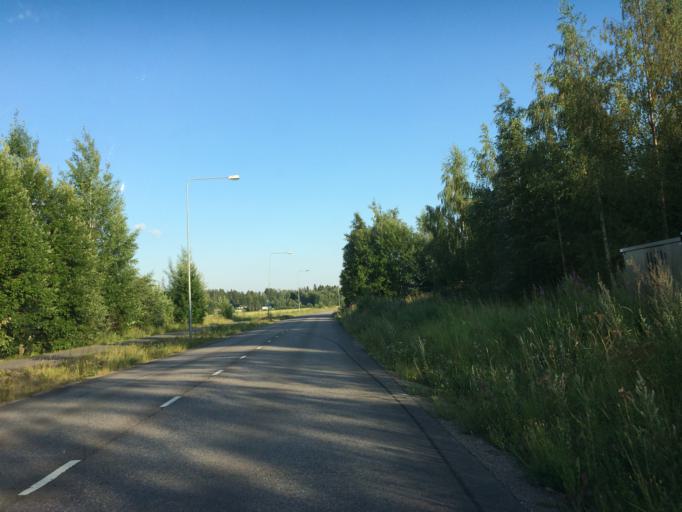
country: FI
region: Haeme
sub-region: Haemeenlinna
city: Parola
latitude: 61.0426
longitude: 24.3794
